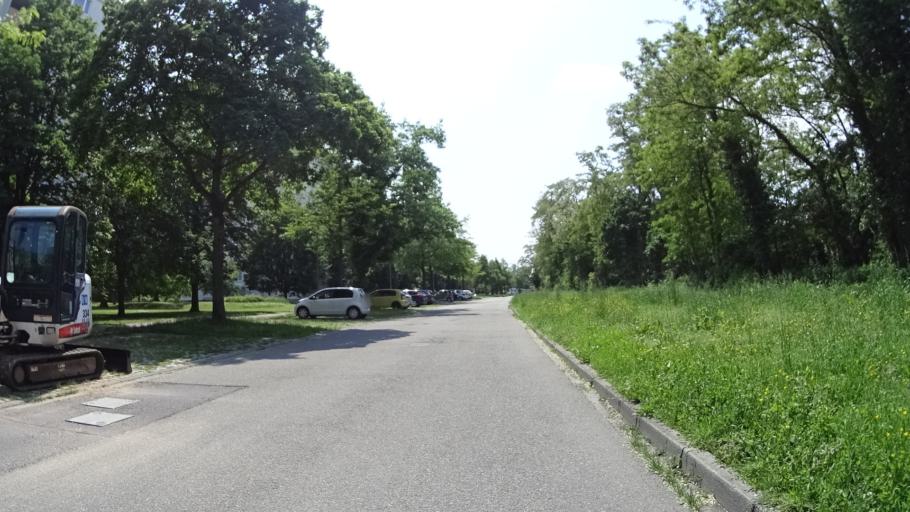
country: DE
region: Baden-Wuerttemberg
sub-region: Karlsruhe Region
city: Rheinstetten
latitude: 48.9955
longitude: 8.3328
